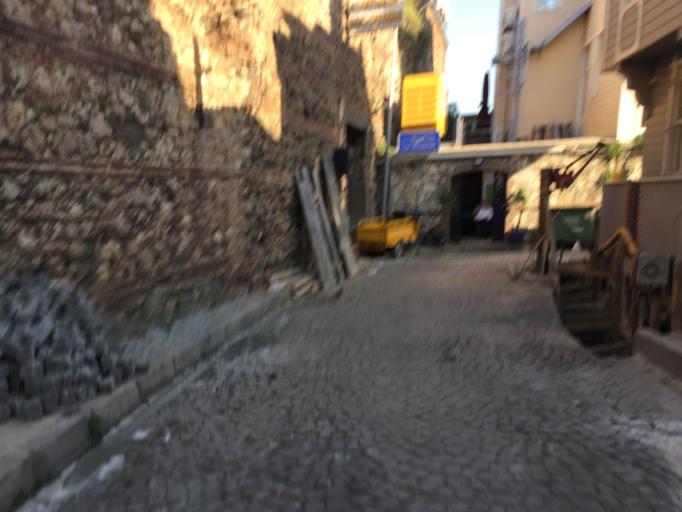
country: TR
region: Istanbul
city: Eminoenue
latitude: 41.0028
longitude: 28.9793
